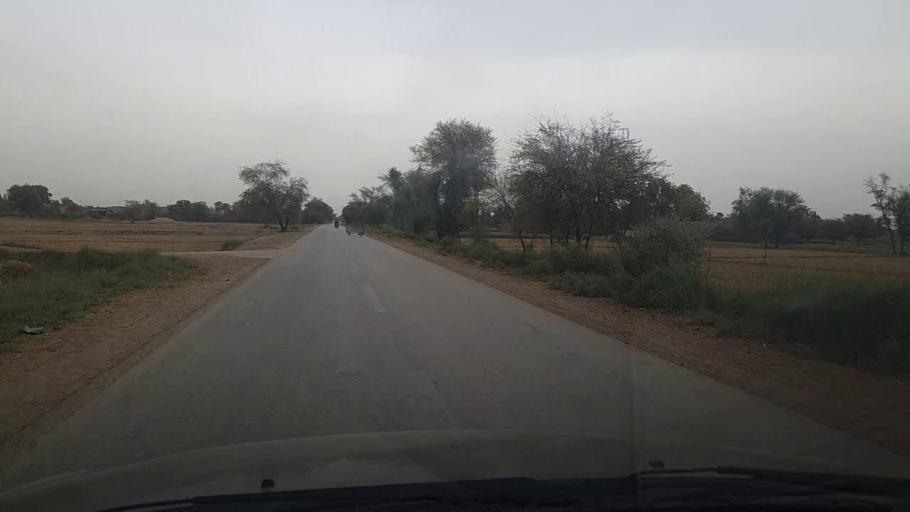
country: PK
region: Sindh
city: Daulatpur
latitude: 26.3249
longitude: 68.1088
